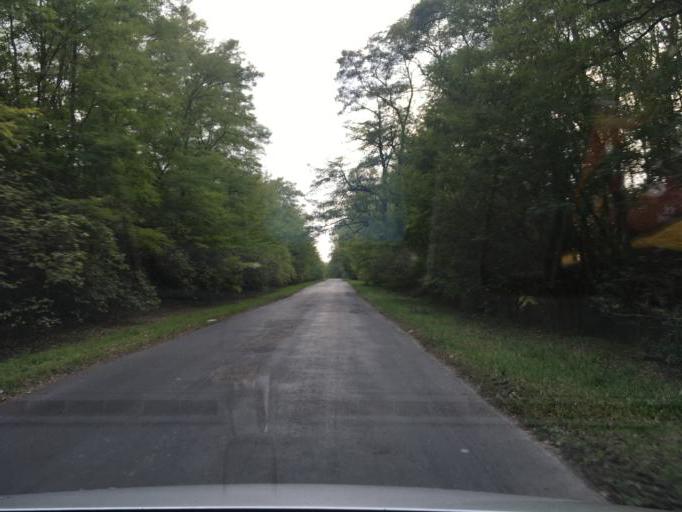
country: HU
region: Gyor-Moson-Sopron
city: Fertod
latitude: 47.6716
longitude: 16.8532
